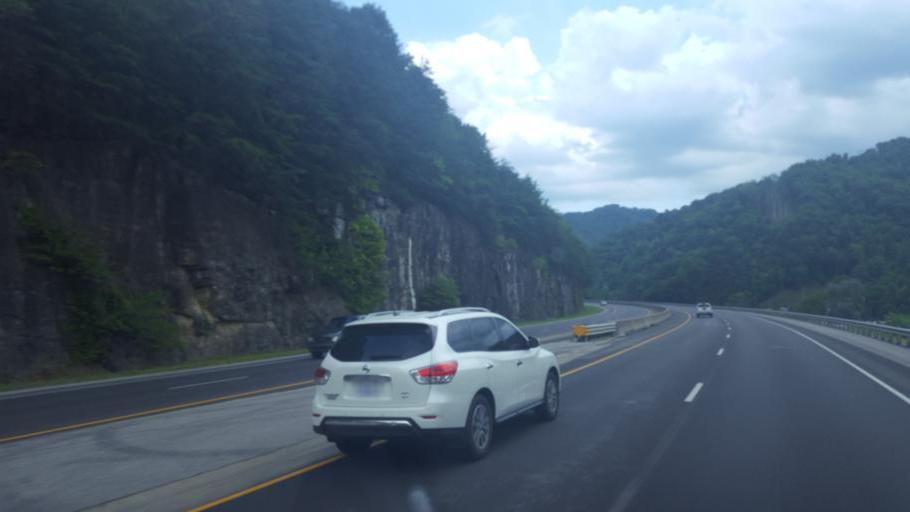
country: US
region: Kentucky
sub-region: Pike County
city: Pikeville
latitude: 37.3553
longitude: -82.5549
